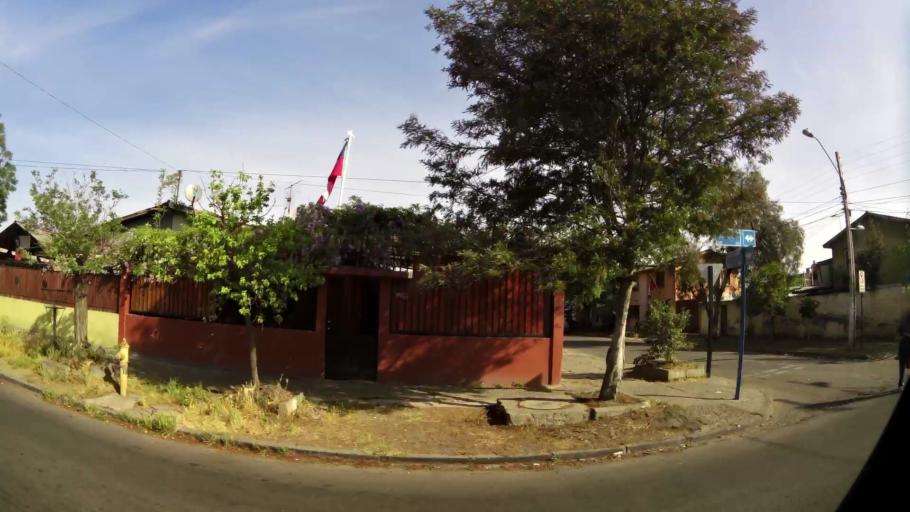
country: CL
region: Santiago Metropolitan
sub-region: Provincia de Santiago
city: La Pintana
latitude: -33.5211
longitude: -70.6344
